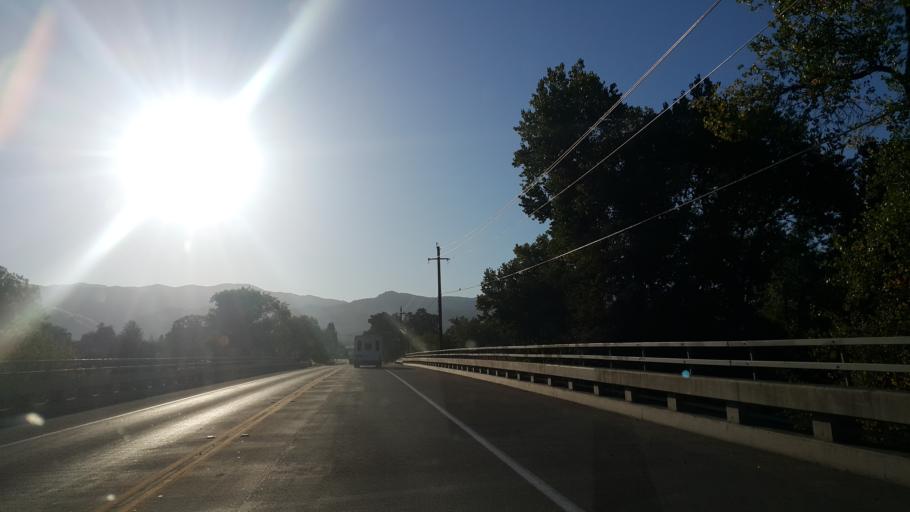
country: US
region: California
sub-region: Mendocino County
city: Talmage
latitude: 39.1346
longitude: -123.1869
